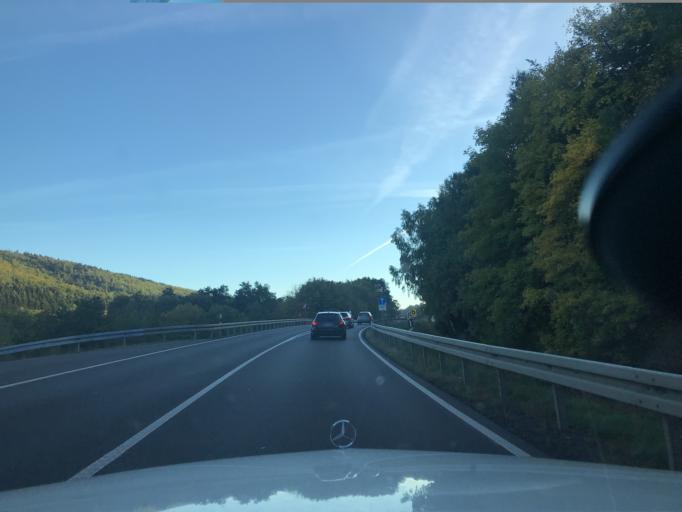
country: DE
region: Hesse
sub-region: Regierungsbezirk Kassel
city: Helsa
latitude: 51.2460
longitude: 9.6831
